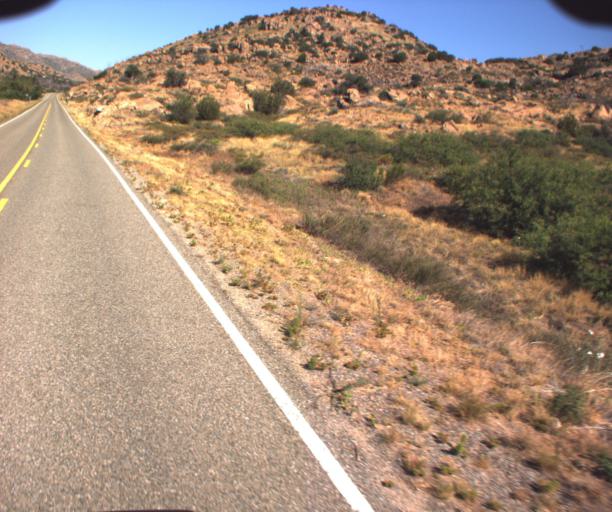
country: US
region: Arizona
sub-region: Graham County
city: Swift Trail Junction
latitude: 32.5621
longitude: -109.7923
